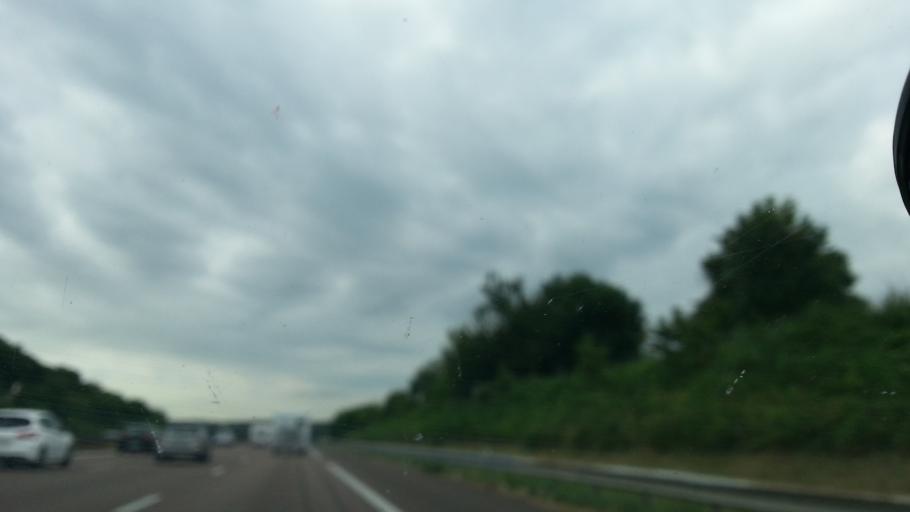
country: FR
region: Bourgogne
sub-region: Departement de Saone-et-Loire
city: Demigny
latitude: 46.9076
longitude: 4.8206
